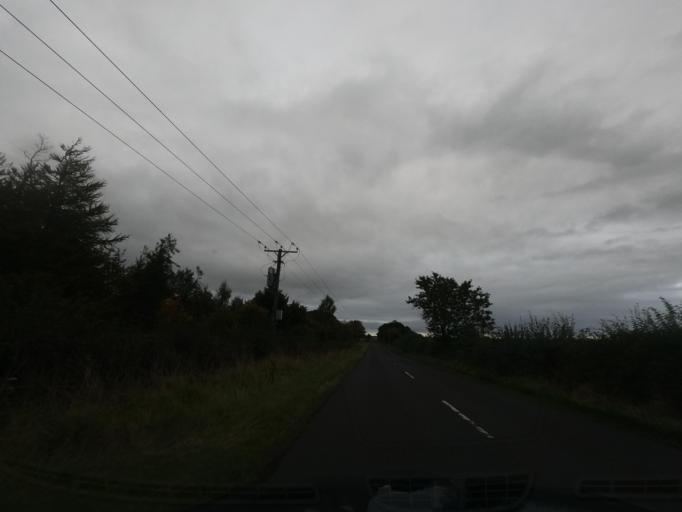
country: GB
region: England
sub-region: Northumberland
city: Ford
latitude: 55.6950
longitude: -2.0744
